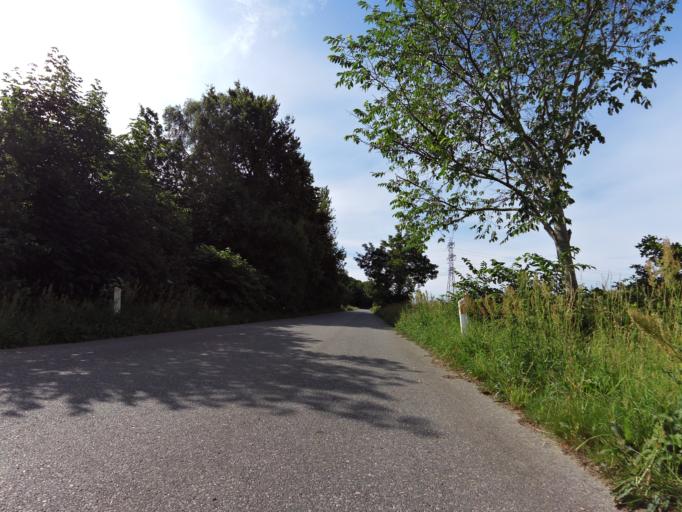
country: DK
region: Central Jutland
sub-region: Arhus Kommune
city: Kolt
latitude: 56.1261
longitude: 10.0801
